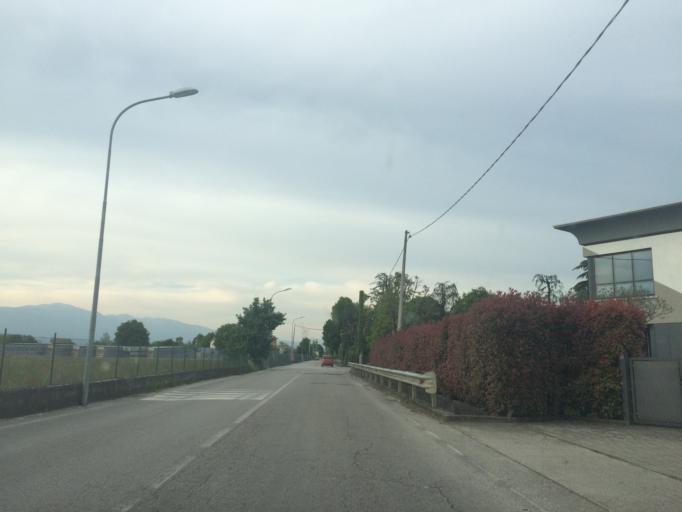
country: IT
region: Veneto
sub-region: Provincia di Vicenza
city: Rossano Veneto
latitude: 45.6862
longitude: 11.7967
